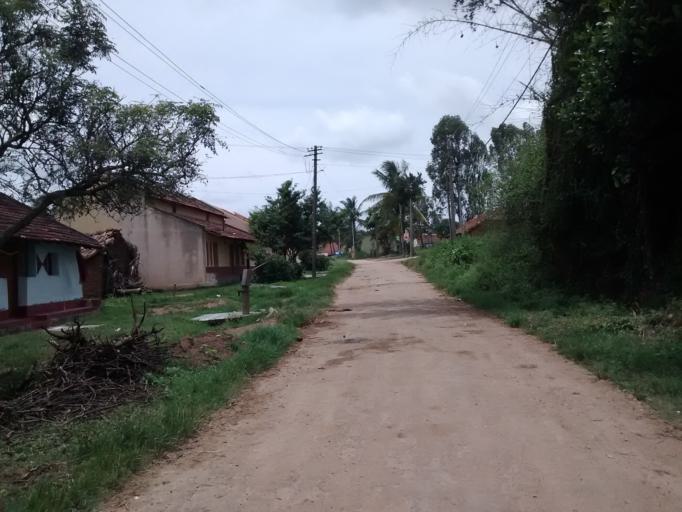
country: IN
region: Karnataka
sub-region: Hassan
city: Hassan
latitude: 12.9086
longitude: 76.1282
